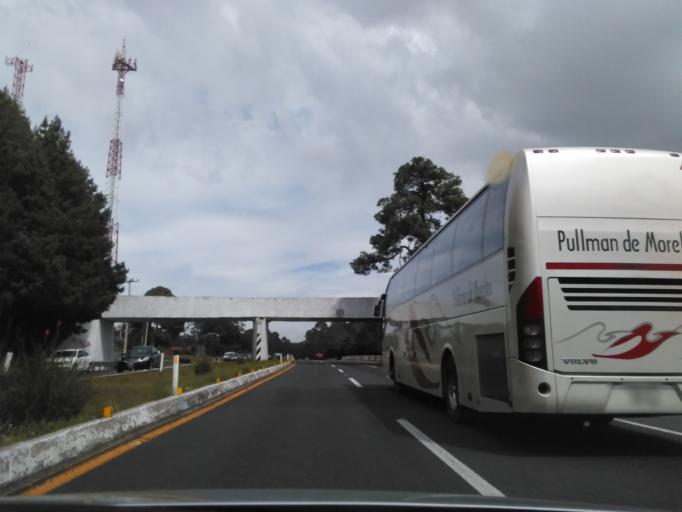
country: MX
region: Morelos
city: Tres Marias
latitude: 19.0881
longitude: -99.2166
